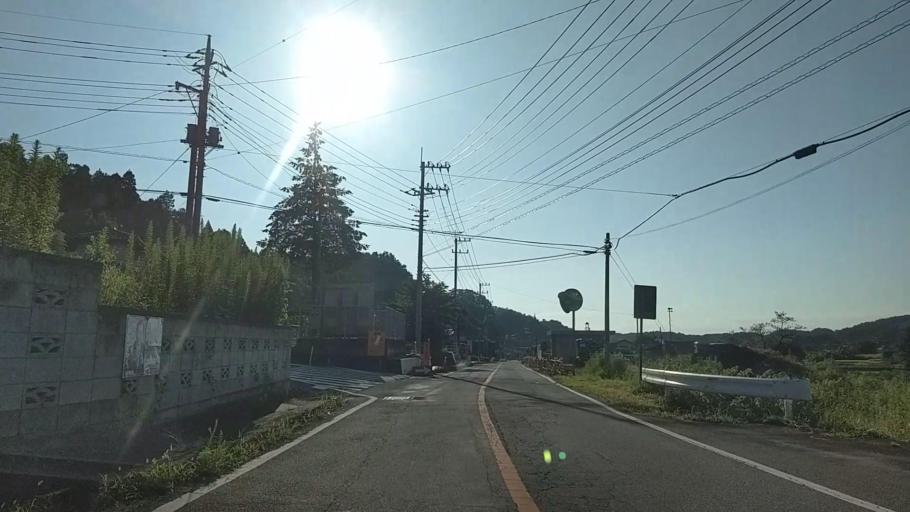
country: JP
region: Gunma
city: Annaka
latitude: 36.3532
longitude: 138.8628
